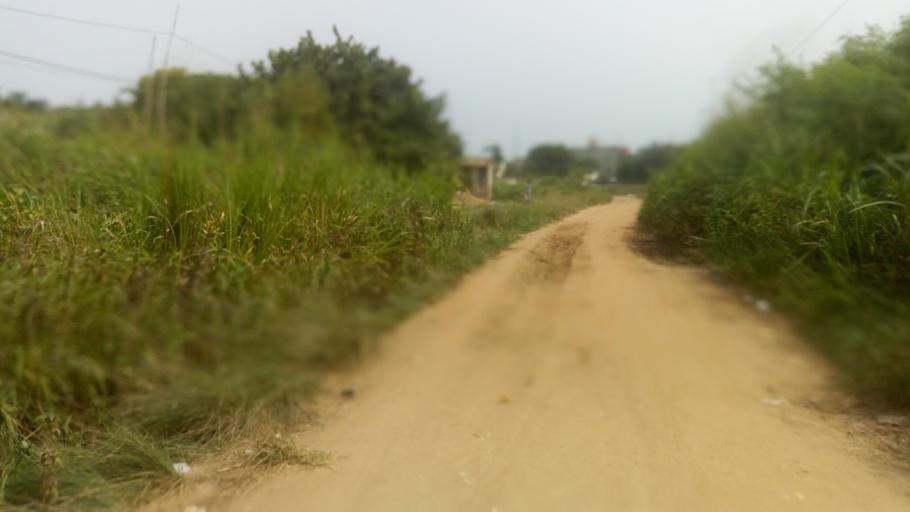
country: TG
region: Maritime
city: Lome
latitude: 6.2798
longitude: 1.2081
